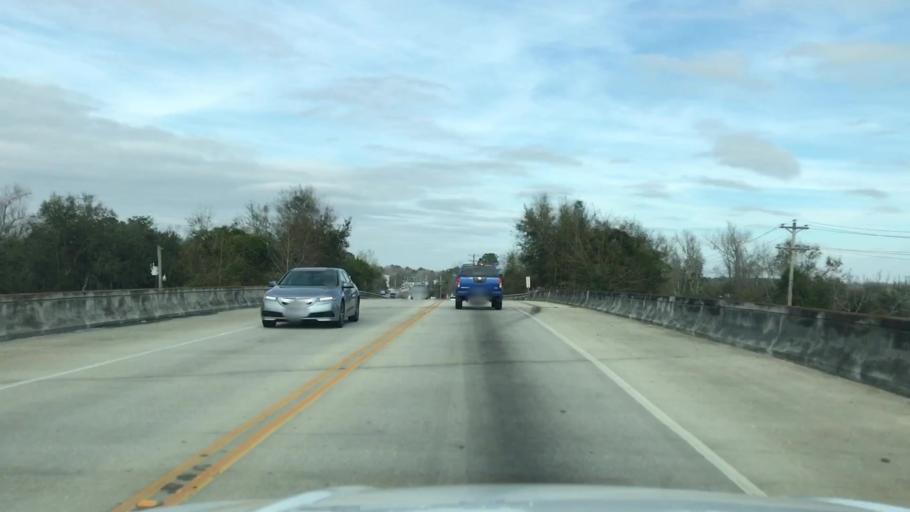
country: US
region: South Carolina
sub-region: Charleston County
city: Shell Point
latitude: 32.7928
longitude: -80.1079
